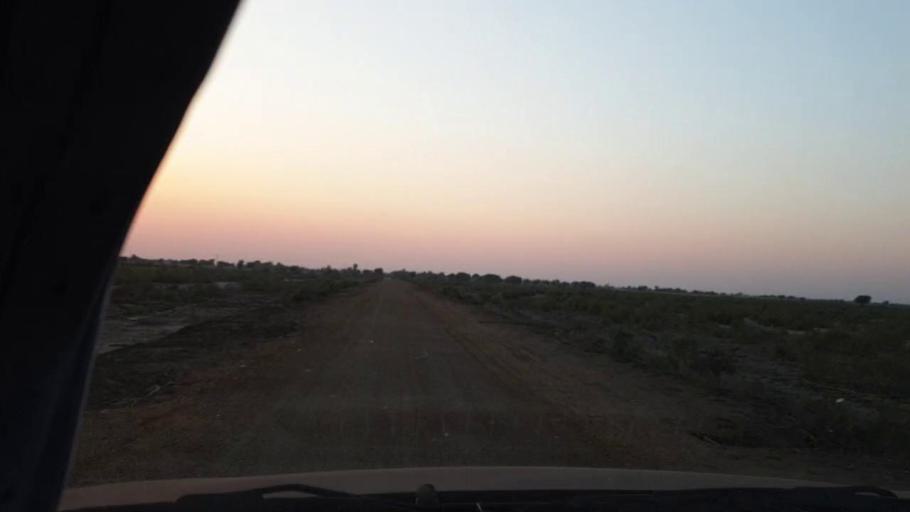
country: PK
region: Sindh
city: Jhol
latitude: 25.9365
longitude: 68.9662
